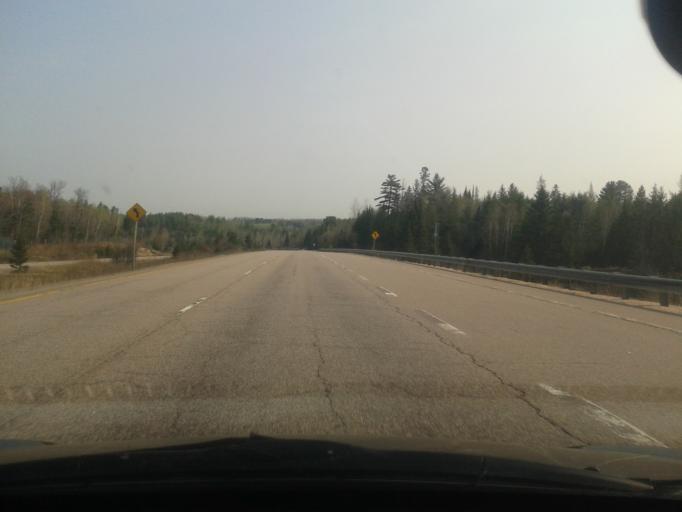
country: CA
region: Ontario
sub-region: Nipissing District
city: North Bay
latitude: 46.2041
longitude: -79.3504
